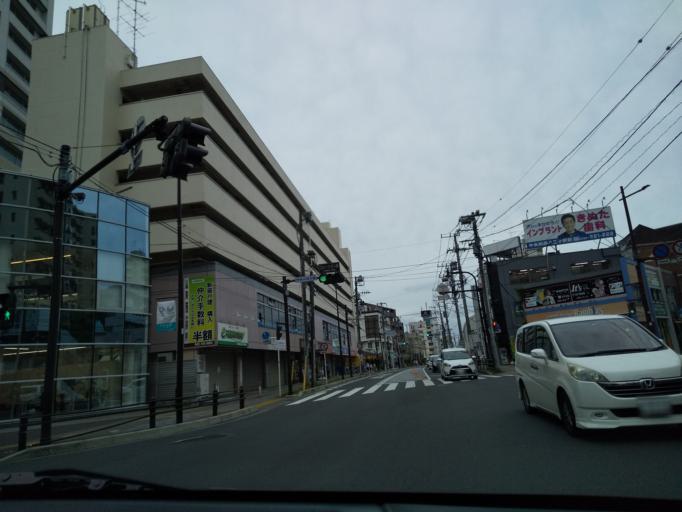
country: JP
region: Tokyo
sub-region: Machida-shi
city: Machida
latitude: 35.5324
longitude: 139.4343
